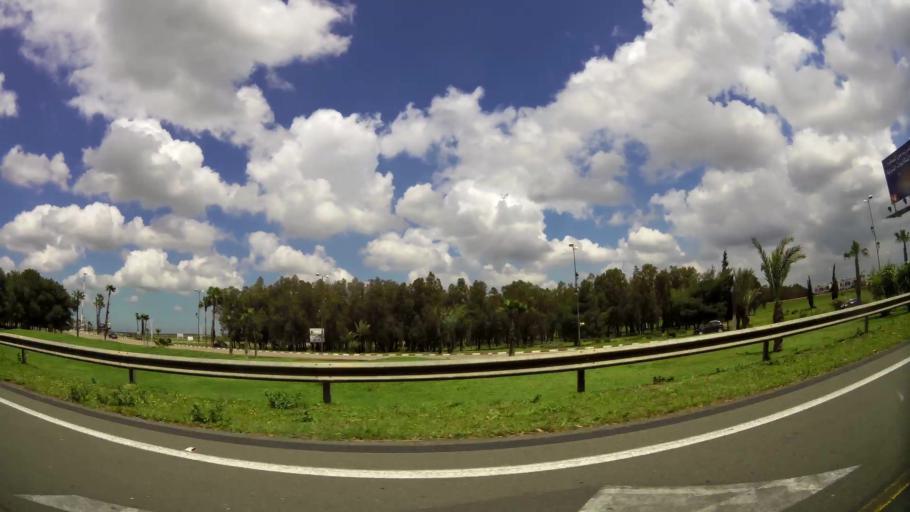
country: MA
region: Chaouia-Ouardigha
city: Nouaseur
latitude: 33.3993
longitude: -7.5701
